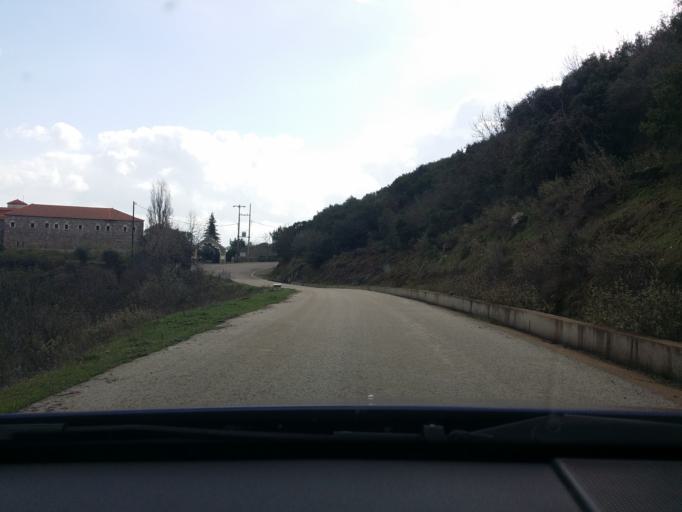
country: GR
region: West Greece
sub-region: Nomos Aitolias kai Akarnanias
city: Fitiai
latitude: 38.6515
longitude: 21.1982
